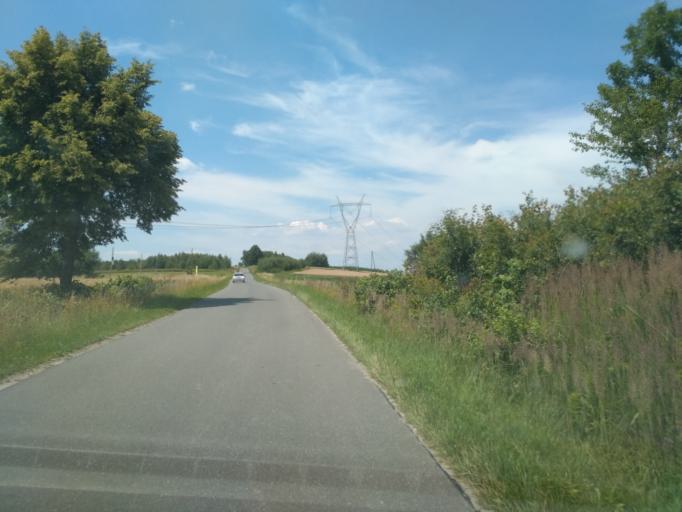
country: PL
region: Subcarpathian Voivodeship
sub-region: Powiat strzyzowski
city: Jawornik
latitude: 49.8666
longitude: 21.8648
